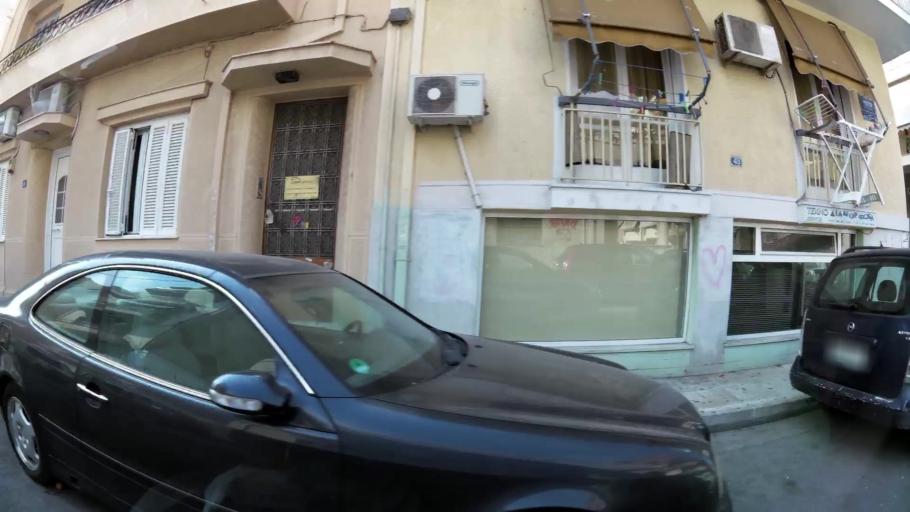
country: GR
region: Attica
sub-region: Nomarchia Athinas
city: Athens
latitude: 37.9920
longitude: 23.7157
